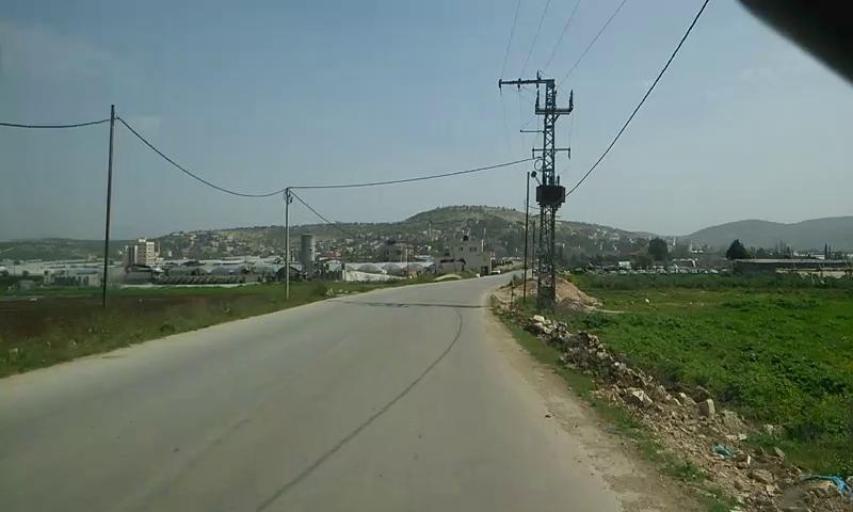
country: PS
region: West Bank
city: Ash Shuhada'
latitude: 32.4341
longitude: 35.2663
